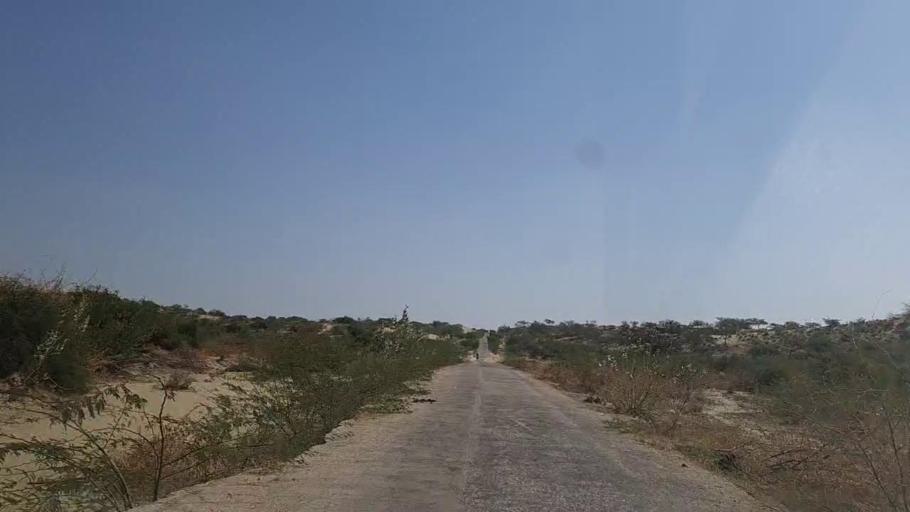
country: PK
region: Sindh
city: Diplo
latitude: 24.4889
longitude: 69.4417
